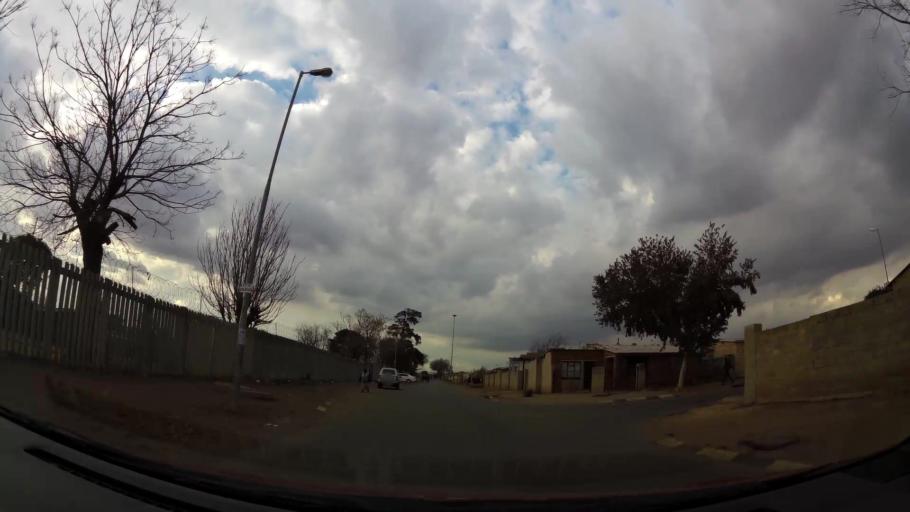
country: ZA
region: Gauteng
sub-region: City of Johannesburg Metropolitan Municipality
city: Soweto
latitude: -26.2403
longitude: 27.8200
